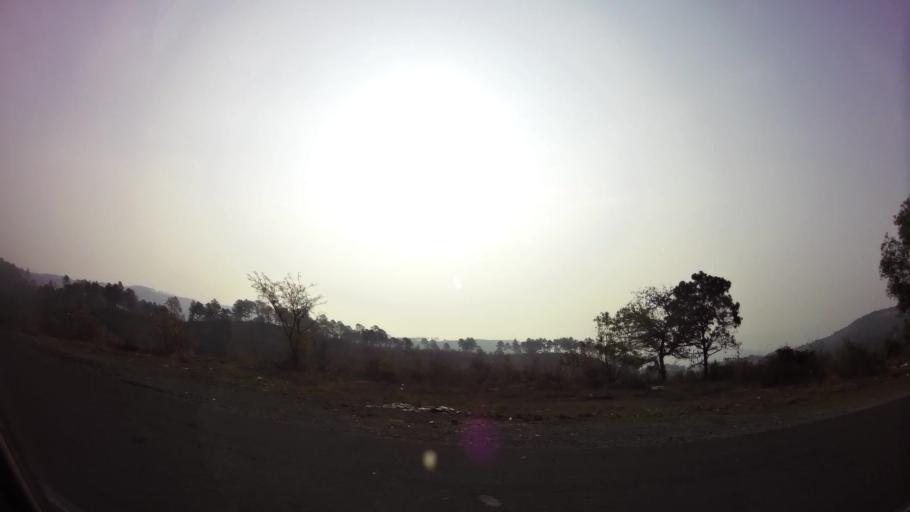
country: HN
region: Francisco Morazan
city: Zambrano
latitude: 14.2602
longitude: -87.3899
